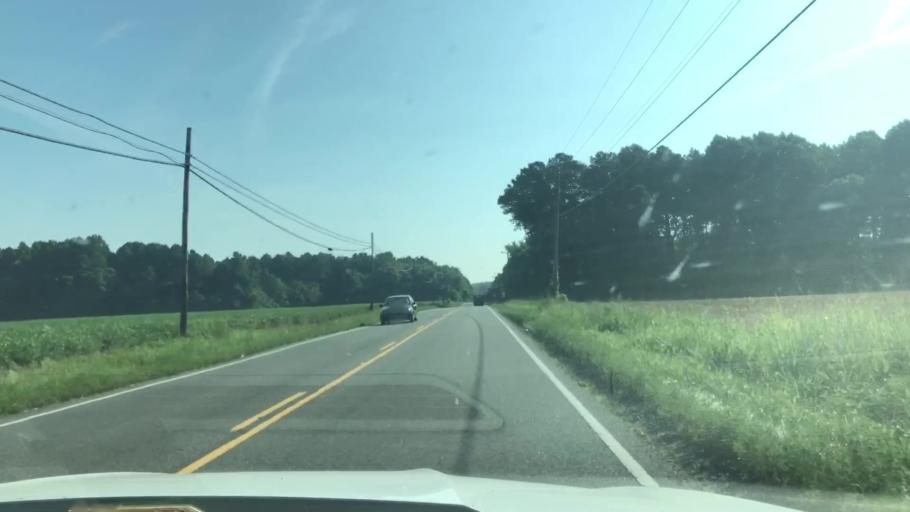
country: US
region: Virginia
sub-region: Richmond County
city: Warsaw
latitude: 37.8920
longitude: -76.6598
